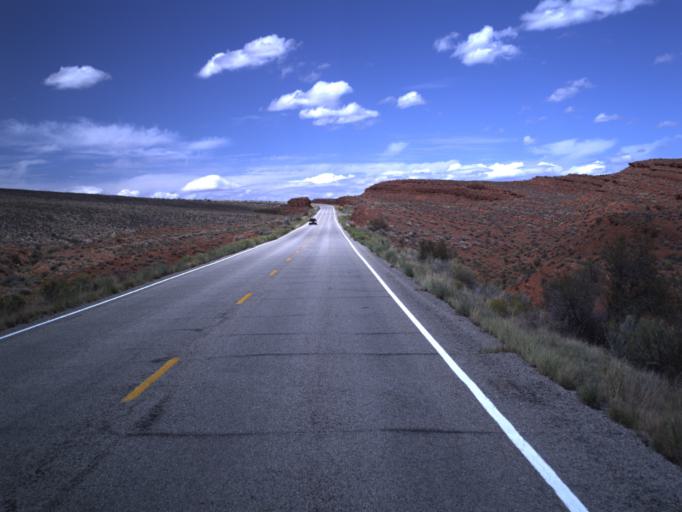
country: US
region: Utah
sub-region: San Juan County
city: Blanding
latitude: 37.2798
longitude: -109.6854
